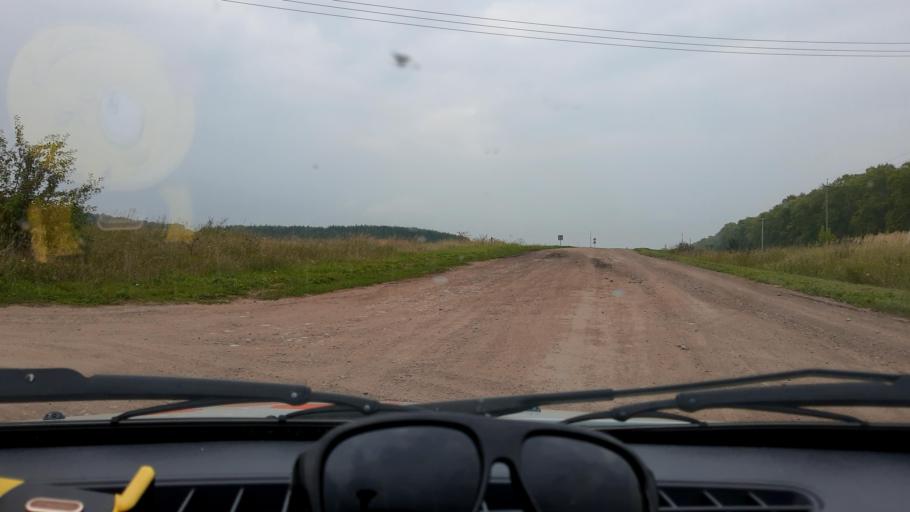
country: RU
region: Bashkortostan
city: Asanovo
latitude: 54.9655
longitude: 55.6142
